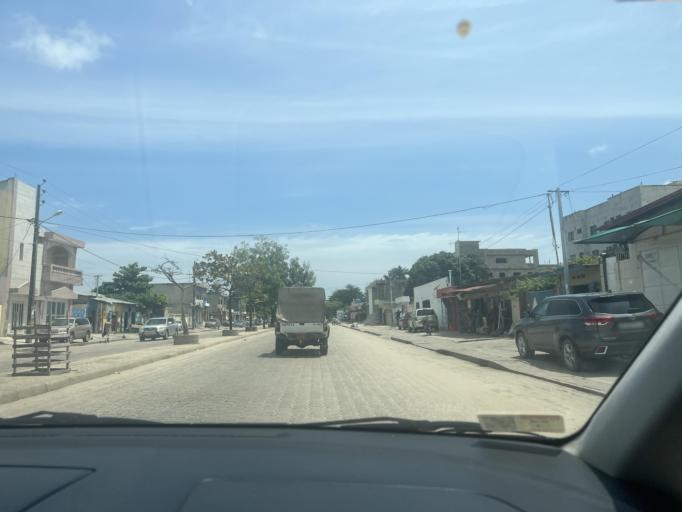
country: BJ
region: Littoral
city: Cotonou
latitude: 6.3765
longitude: 2.4468
